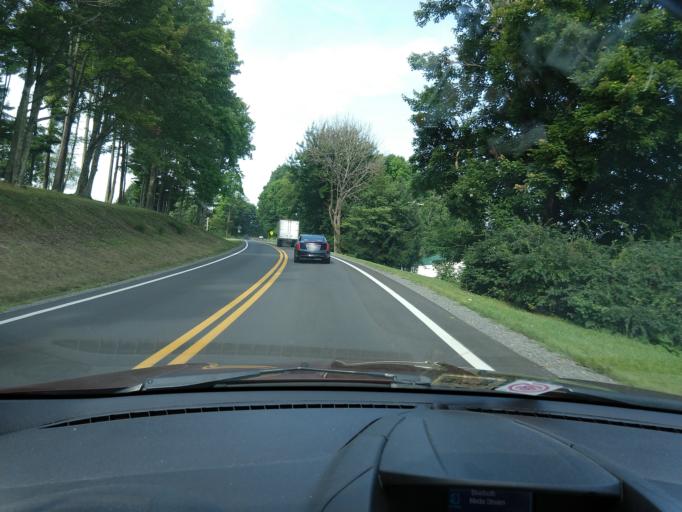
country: US
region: West Virginia
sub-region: Nicholas County
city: Craigsville
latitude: 38.2313
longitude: -80.7032
